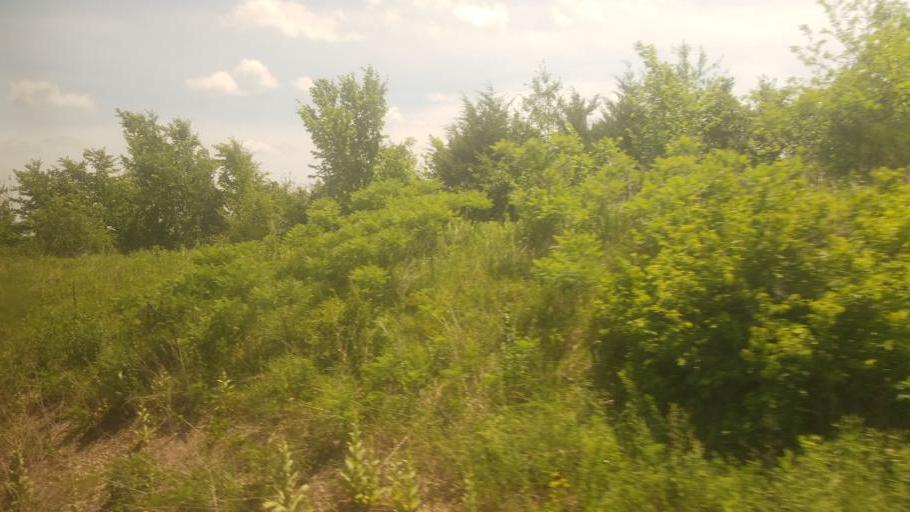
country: US
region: Missouri
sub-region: Linn County
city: Marceline
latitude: 39.8450
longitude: -92.8179
